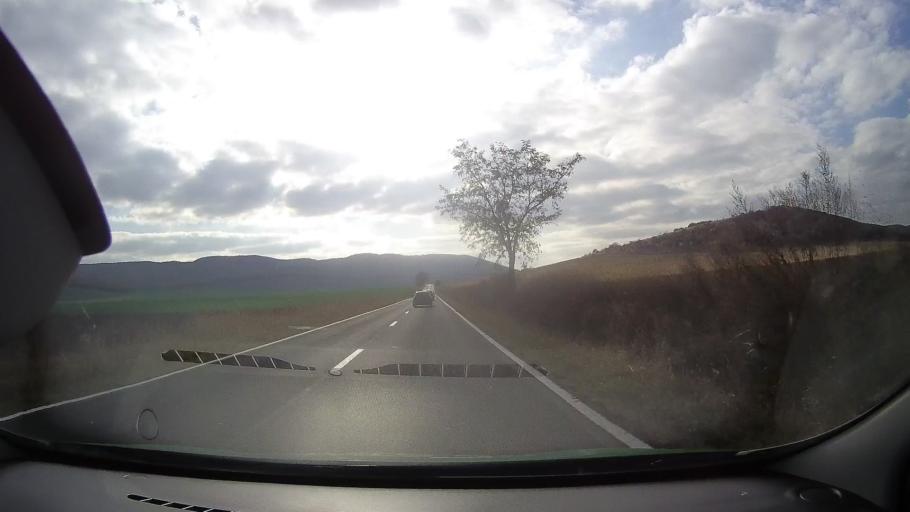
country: RO
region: Tulcea
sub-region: Comuna Nalbant
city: Nicolae Balcescu
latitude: 44.9740
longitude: 28.5426
